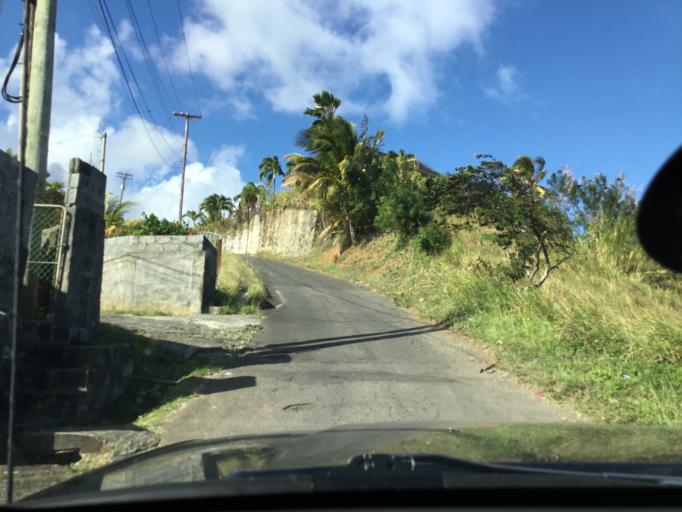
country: VC
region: Saint George
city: Kingstown
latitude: 13.1505
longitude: -61.1789
